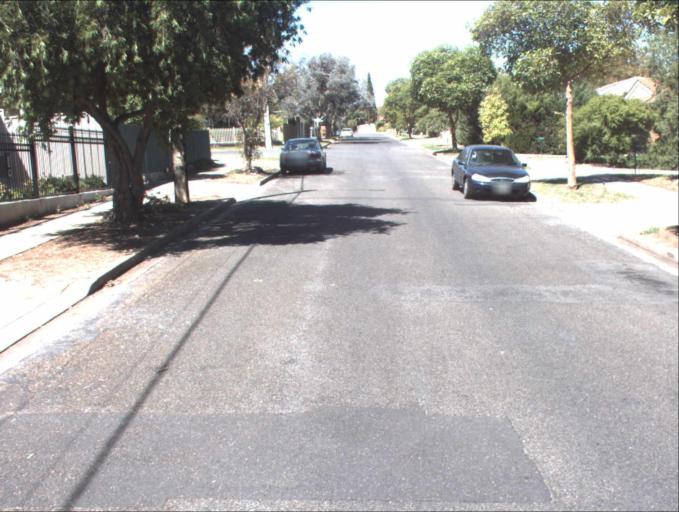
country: AU
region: South Australia
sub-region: Port Adelaide Enfield
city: Blair Athol
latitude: -34.8624
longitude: 138.6056
